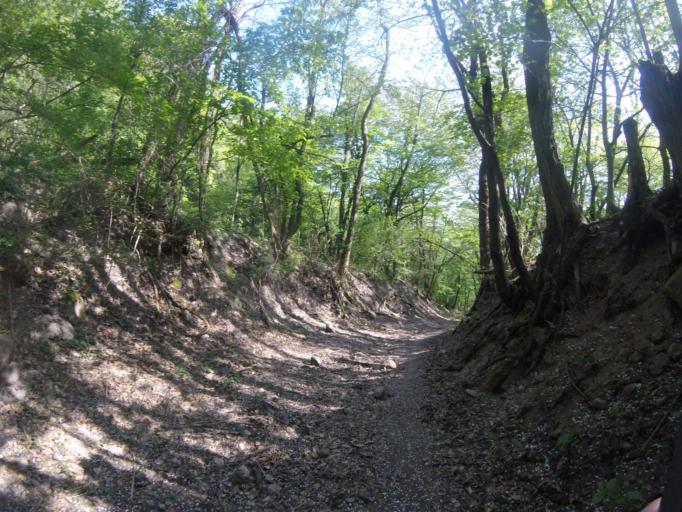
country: HU
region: Pest
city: Pilisszentkereszt
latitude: 47.7042
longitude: 18.8989
